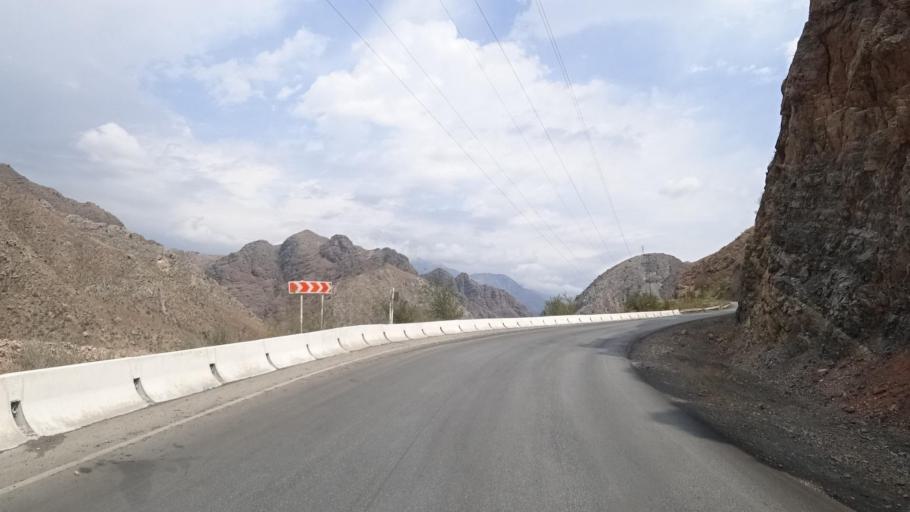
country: KG
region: Jalal-Abad
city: Tash-Kumyr
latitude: 41.5715
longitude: 72.5288
